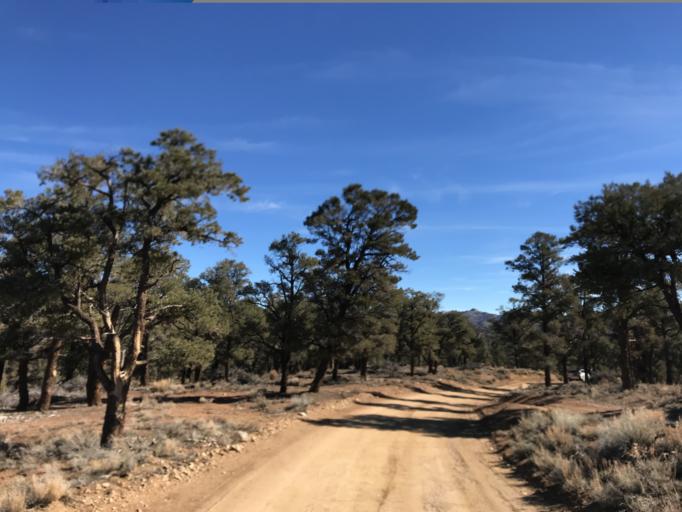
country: US
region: California
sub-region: San Bernardino County
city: Big Bear City
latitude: 34.2687
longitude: -116.7634
